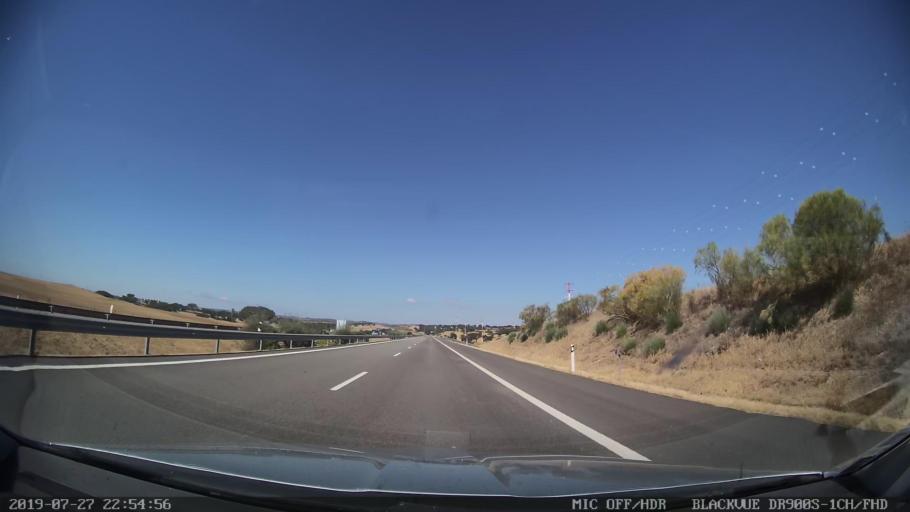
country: PT
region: Evora
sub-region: Vila Vicosa
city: Vila Vicosa
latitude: 38.8481
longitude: -7.3693
